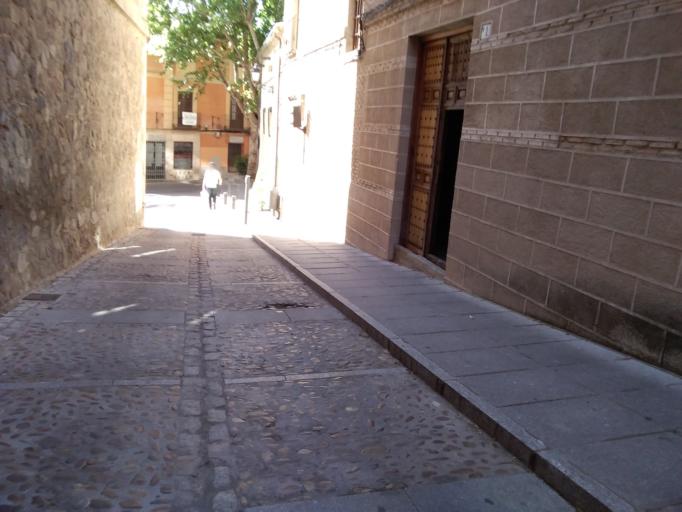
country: ES
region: Castille-La Mancha
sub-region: Province of Toledo
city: Toledo
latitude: 39.8582
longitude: -4.0263
